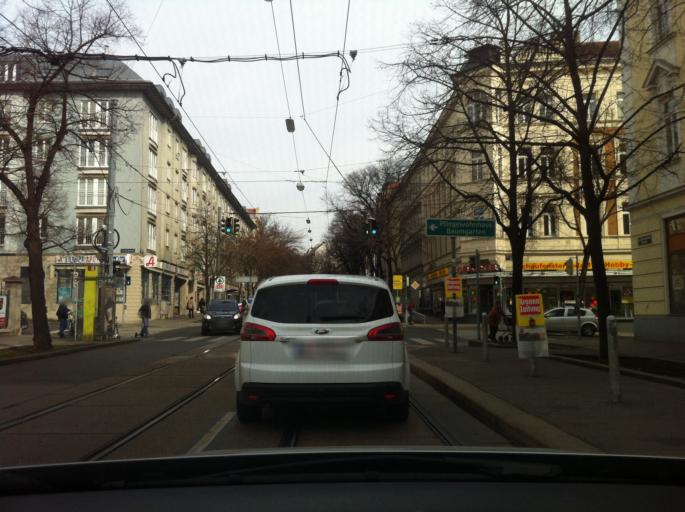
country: AT
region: Lower Austria
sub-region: Politischer Bezirk Modling
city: Perchtoldsdorf
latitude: 48.1967
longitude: 16.2867
